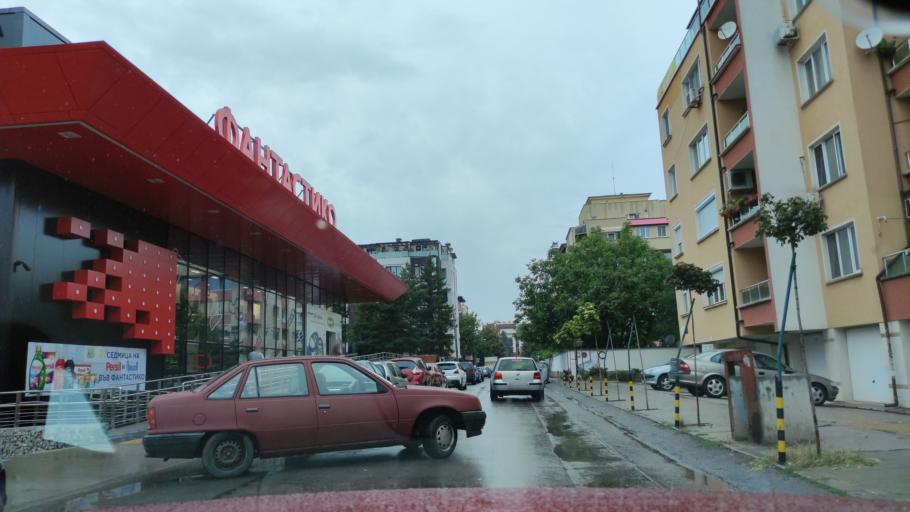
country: BG
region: Sofia-Capital
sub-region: Stolichna Obshtina
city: Sofia
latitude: 42.6656
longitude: 23.2805
